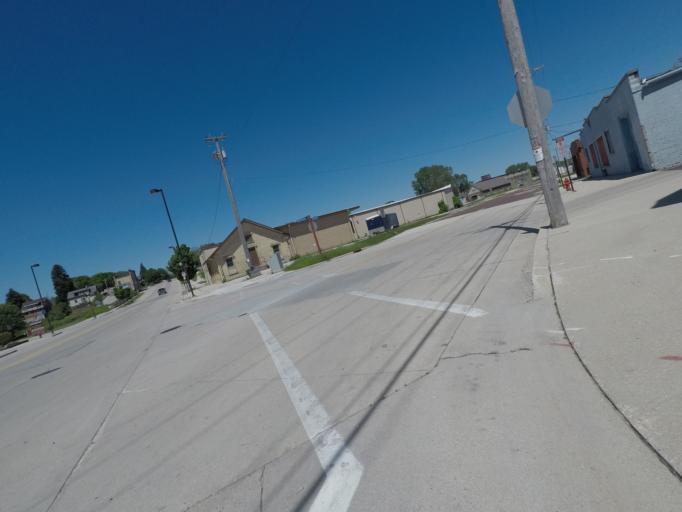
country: US
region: Wisconsin
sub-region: Sheboygan County
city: Sheboygan
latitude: 43.7499
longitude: -87.7186
